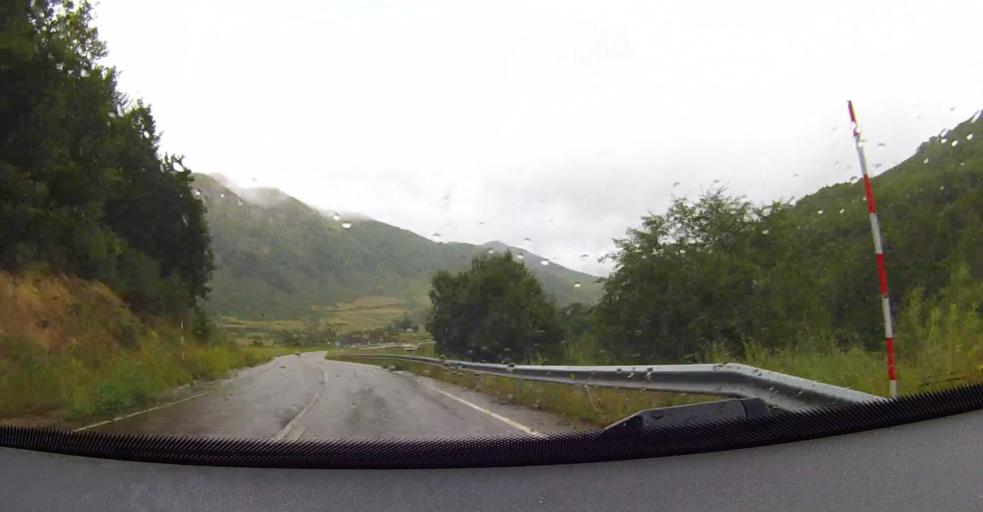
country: ES
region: Castille and Leon
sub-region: Provincia de Leon
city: Marana
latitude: 43.0720
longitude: -5.1597
